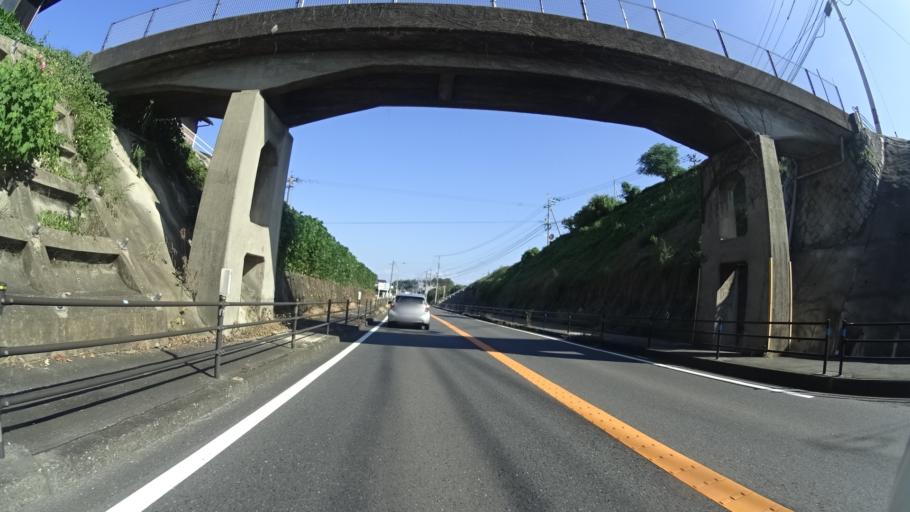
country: JP
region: Fukuoka
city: Shiida
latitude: 33.6247
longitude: 131.0894
